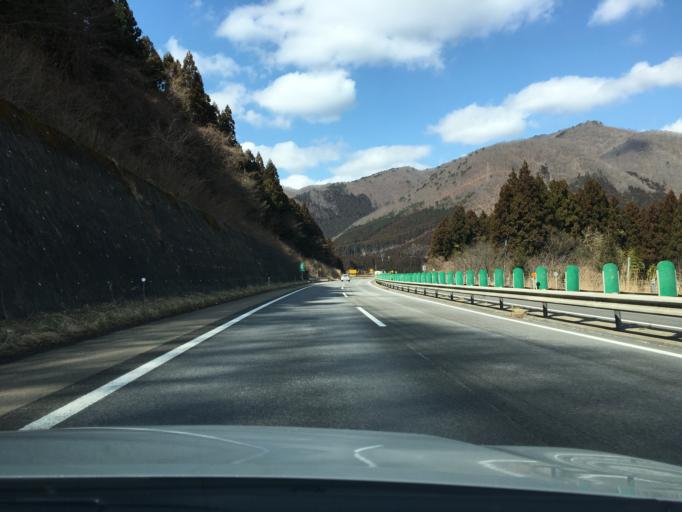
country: JP
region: Miyagi
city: Shiroishi
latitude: 38.2013
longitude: 140.5816
